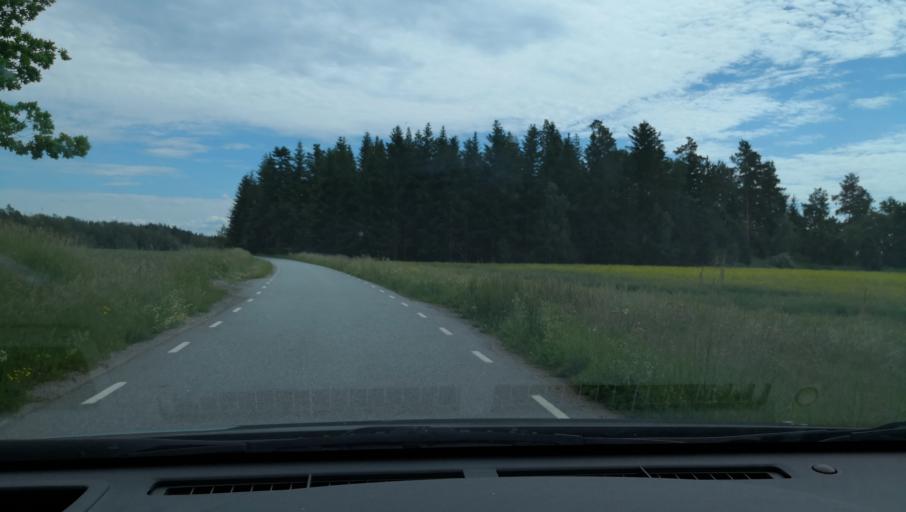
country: SE
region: Uppsala
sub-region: Enkopings Kommun
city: Orsundsbro
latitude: 59.7000
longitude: 17.4295
